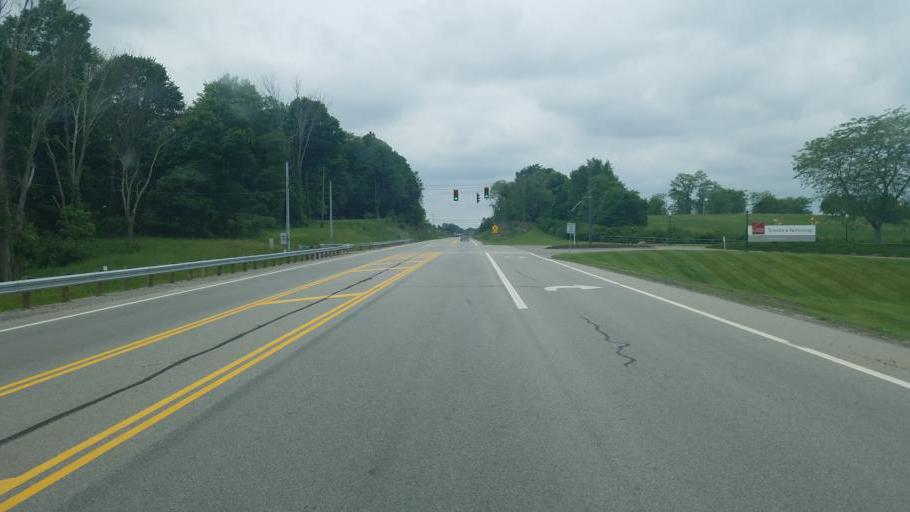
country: US
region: Ohio
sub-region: Licking County
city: Granville South
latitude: 40.0518
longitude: -82.5516
